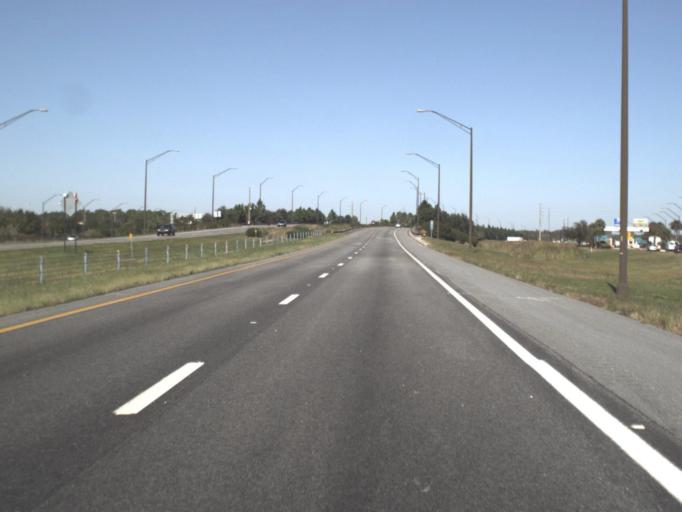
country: US
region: Florida
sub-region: Hillsborough County
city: Cheval
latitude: 28.1856
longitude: -82.5408
